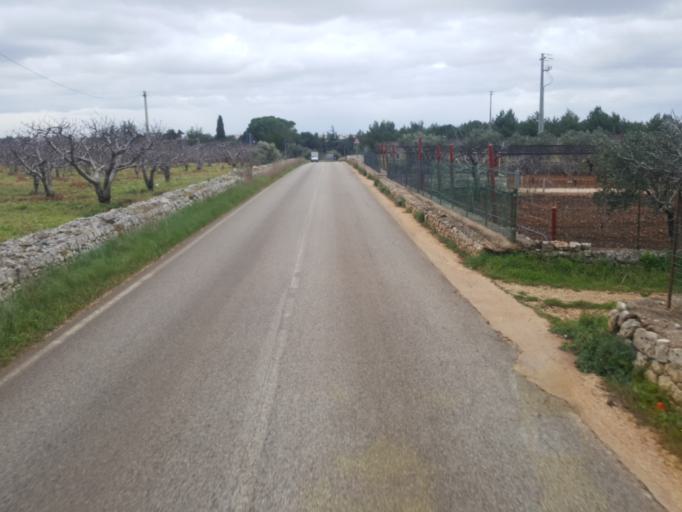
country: IT
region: Apulia
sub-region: Provincia di Bari
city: Turi
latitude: 40.9236
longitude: 17.0421
